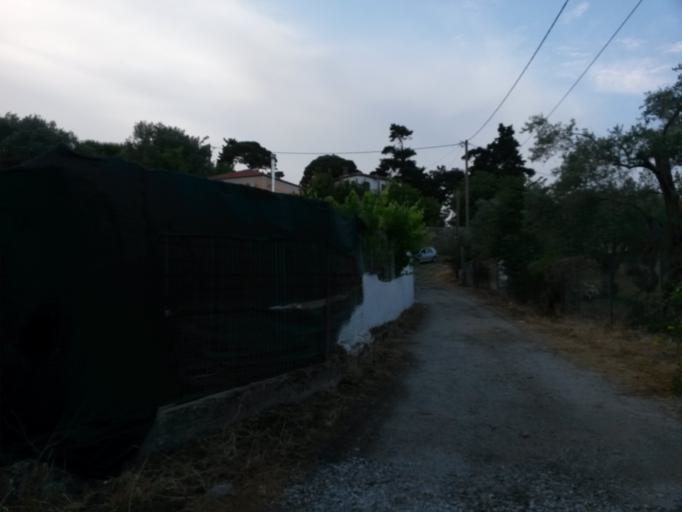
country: GR
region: North Aegean
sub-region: Nomos Lesvou
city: Pamfylla
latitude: 39.1740
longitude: 26.4989
